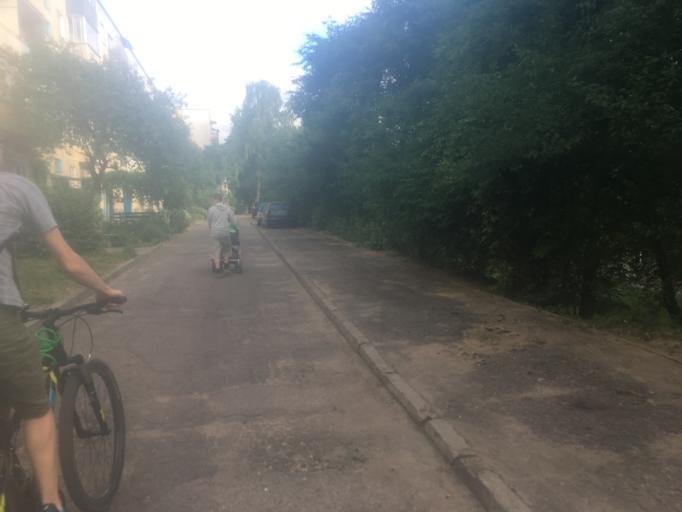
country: BY
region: Grodnenskaya
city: Hrodna
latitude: 53.7007
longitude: 23.8051
